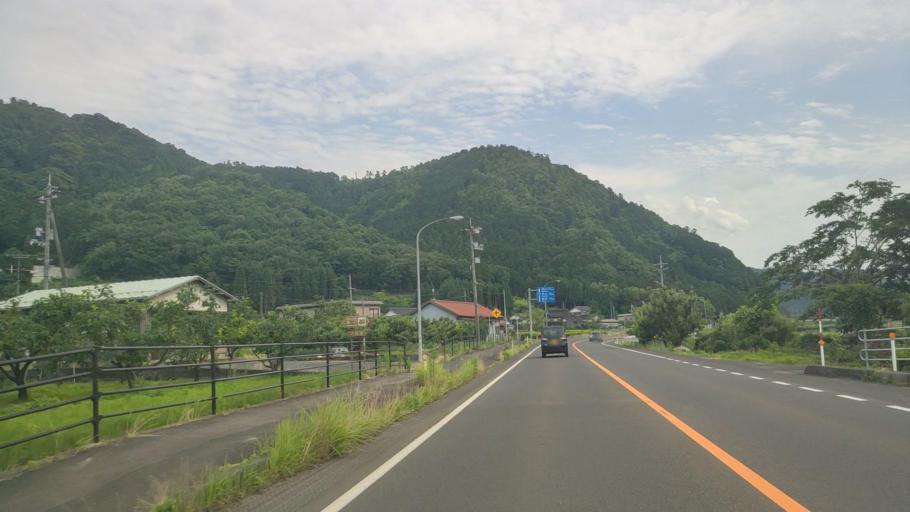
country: JP
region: Tottori
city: Tottori
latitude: 35.3697
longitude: 134.2155
